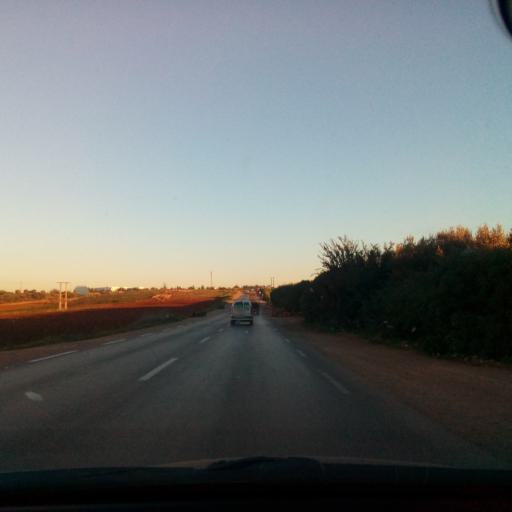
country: DZ
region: Relizane
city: Relizane
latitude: 35.7361
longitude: 0.2967
